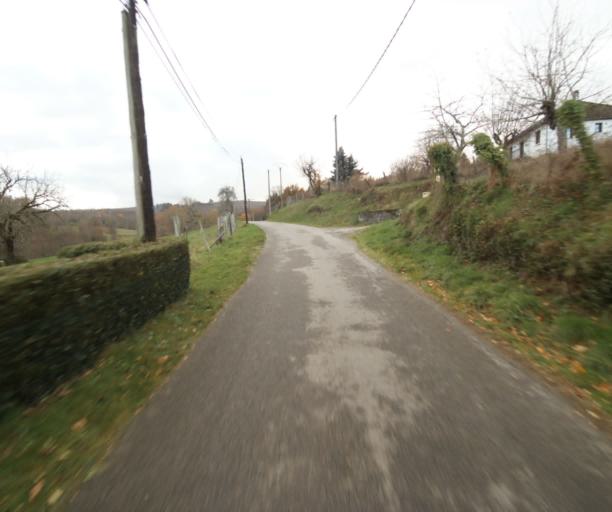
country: FR
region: Limousin
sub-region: Departement de la Correze
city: Sainte-Fortunade
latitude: 45.2210
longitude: 1.7838
